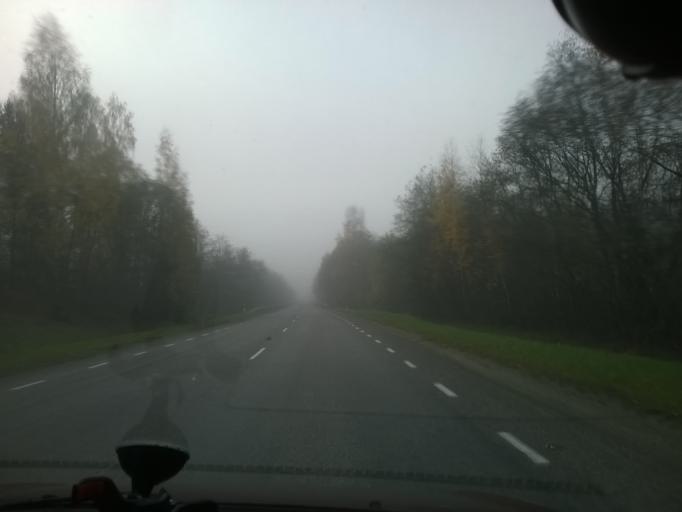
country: EE
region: Tartu
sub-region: Noo vald
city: Noo
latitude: 58.1507
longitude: 26.5264
